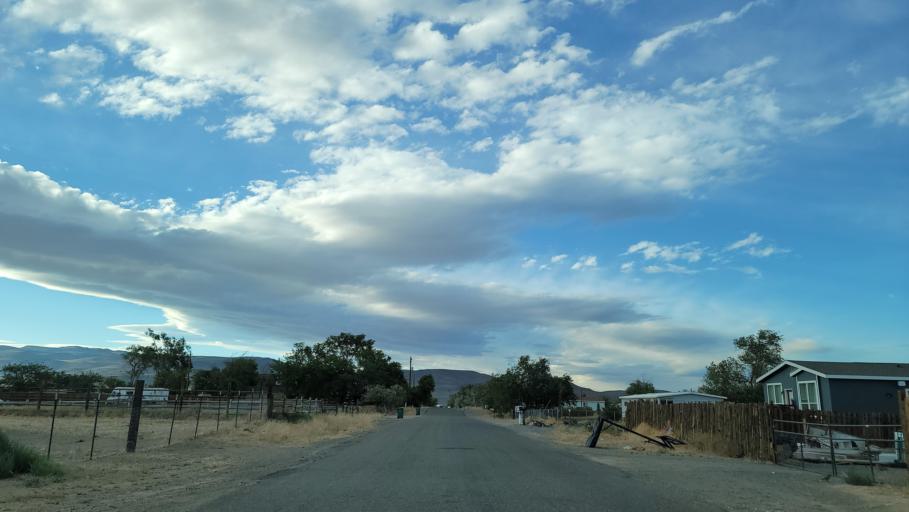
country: US
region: Nevada
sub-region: Lyon County
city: Silver Springs
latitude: 39.3902
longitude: -119.2376
